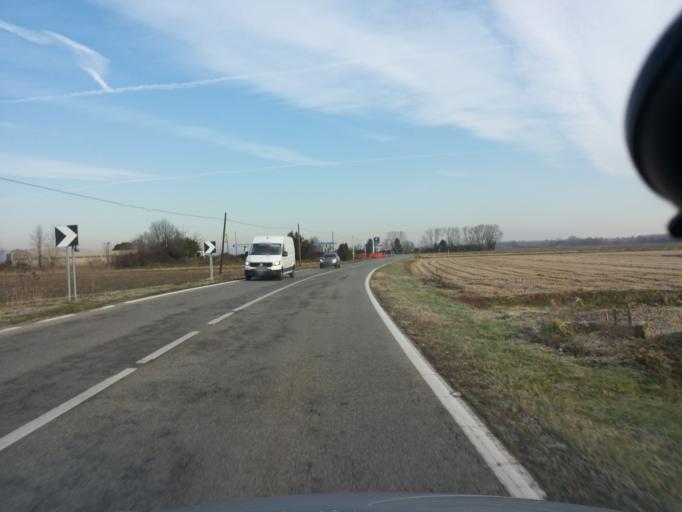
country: IT
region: Piedmont
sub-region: Provincia di Vercelli
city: Oldenico
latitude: 45.3896
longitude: 8.3767
